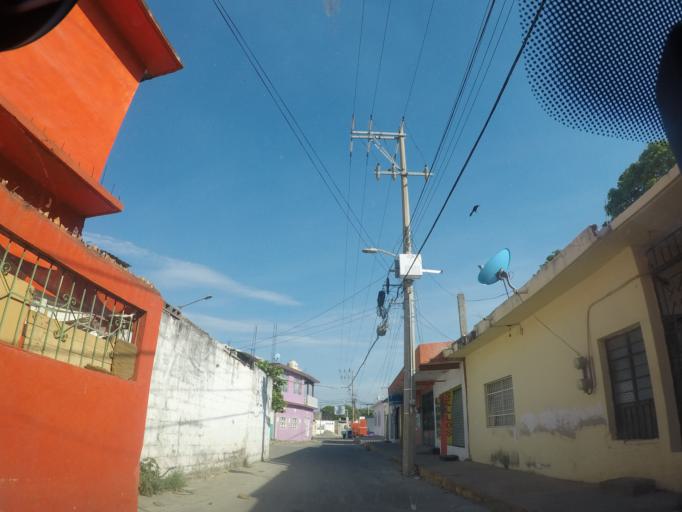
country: MX
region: Oaxaca
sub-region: Salina Cruz
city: Salina Cruz
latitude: 16.1771
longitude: -95.1979
